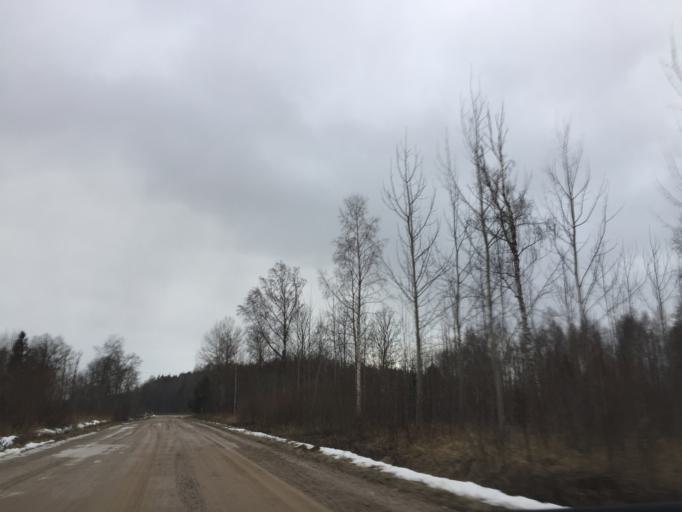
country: LV
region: Salacgrivas
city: Salacgriva
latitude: 57.6492
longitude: 24.4056
